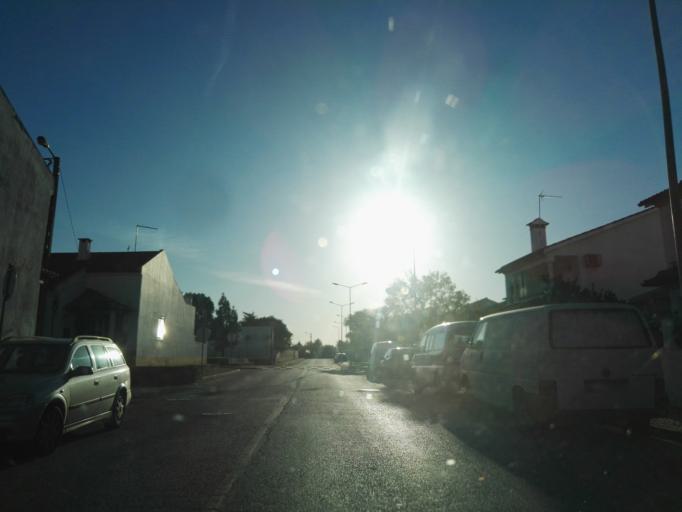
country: PT
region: Santarem
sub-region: Golega
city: Golega
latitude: 39.4096
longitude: -8.4910
